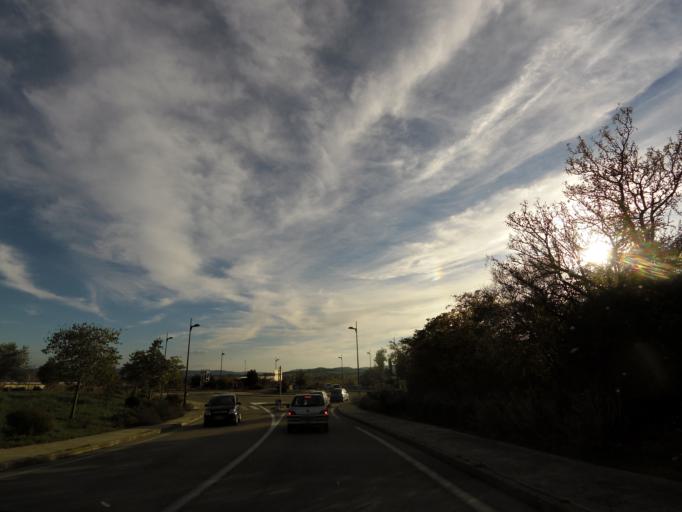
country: FR
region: Languedoc-Roussillon
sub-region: Departement du Gard
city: Ledignan
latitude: 43.9845
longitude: 4.1052
